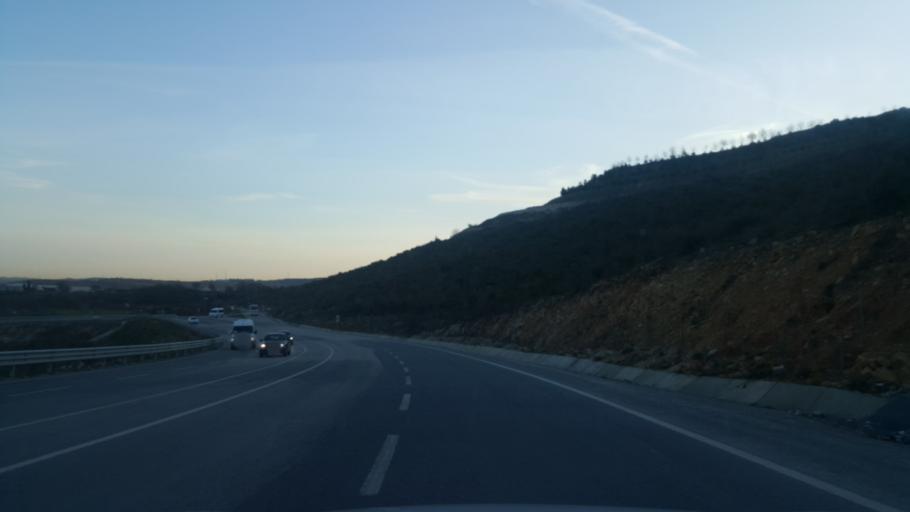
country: TR
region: Kocaeli
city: Tavsanli
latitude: 40.8386
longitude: 29.5515
